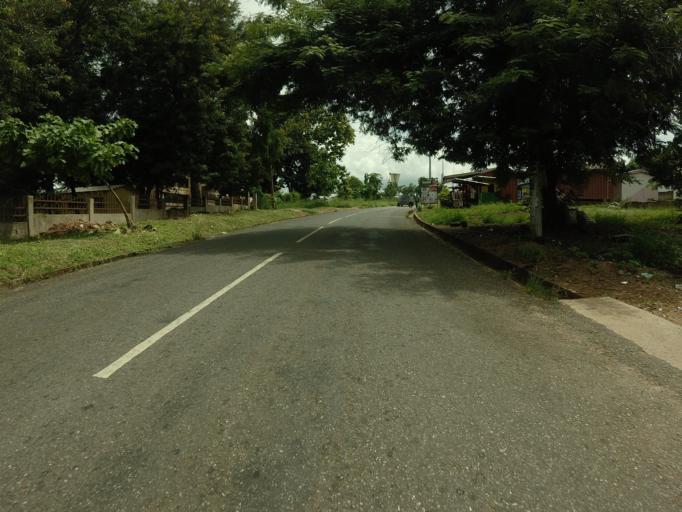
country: GH
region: Volta
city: Ho
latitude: 6.5922
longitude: 0.4686
